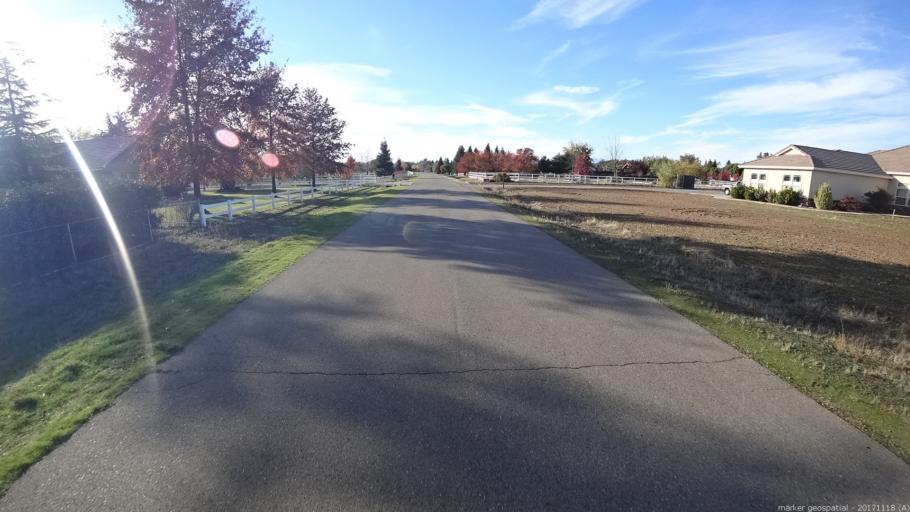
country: US
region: California
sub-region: Shasta County
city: Cottonwood
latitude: 40.3761
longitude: -122.3417
